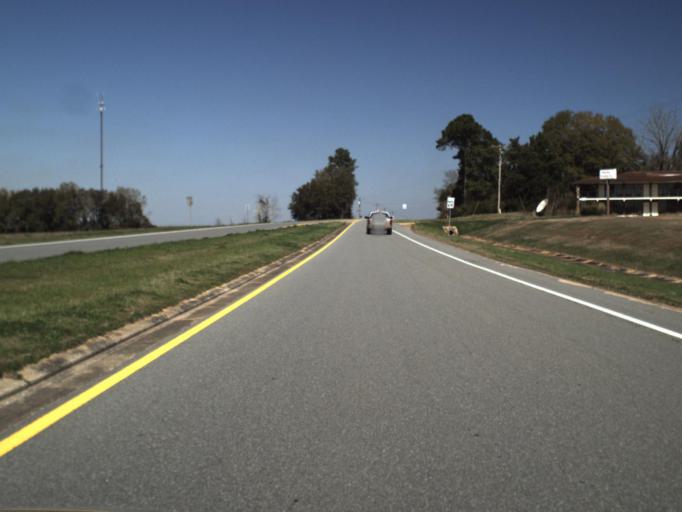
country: US
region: Florida
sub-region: Jackson County
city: Sneads
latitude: 30.6619
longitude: -85.0387
